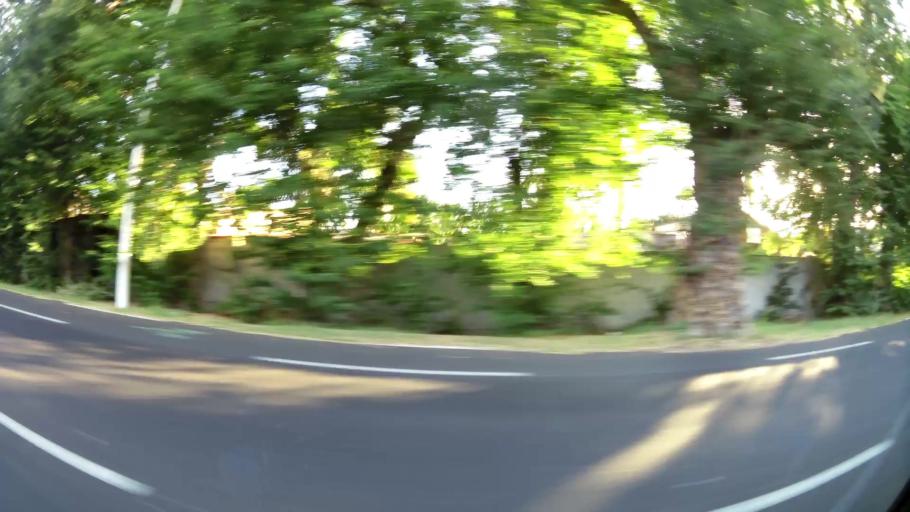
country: RE
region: Reunion
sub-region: Reunion
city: Trois-Bassins
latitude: -21.0787
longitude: 55.2288
